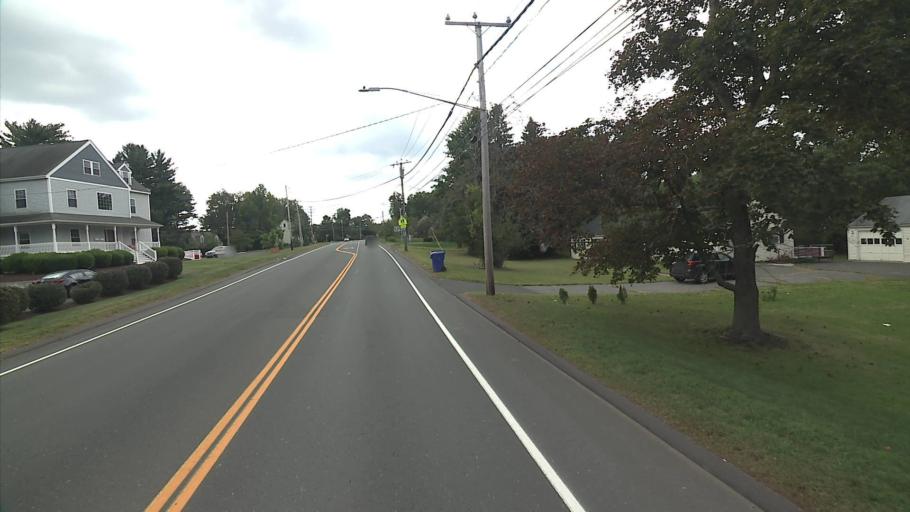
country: US
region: Connecticut
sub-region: Hartford County
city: Blue Hills
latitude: 41.8260
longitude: -72.7375
